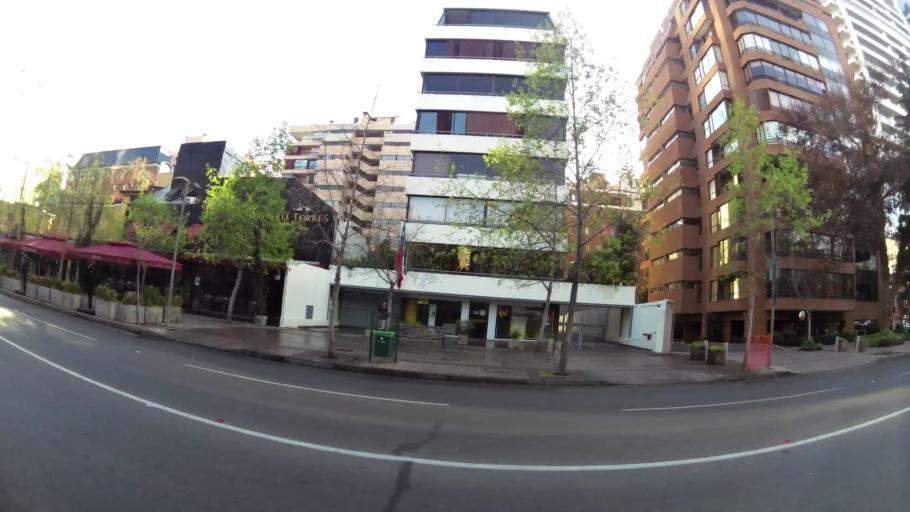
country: CL
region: Santiago Metropolitan
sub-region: Provincia de Santiago
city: Villa Presidente Frei, Nunoa, Santiago, Chile
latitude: -33.4142
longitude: -70.5995
